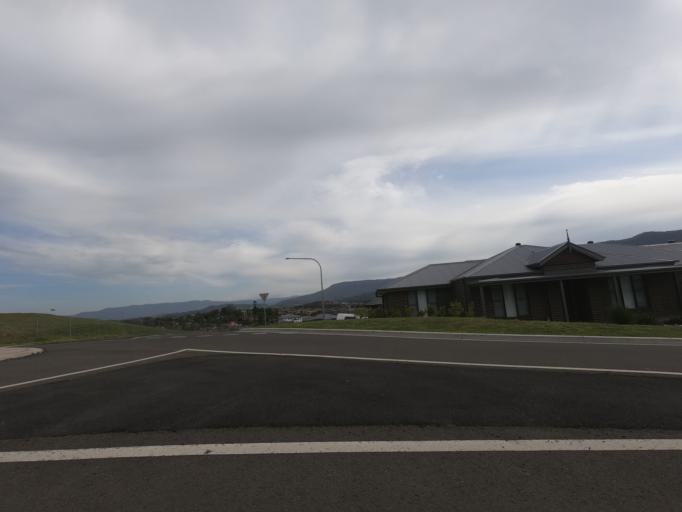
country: AU
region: New South Wales
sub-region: Wollongong
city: Dapto
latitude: -34.4800
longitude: 150.7840
